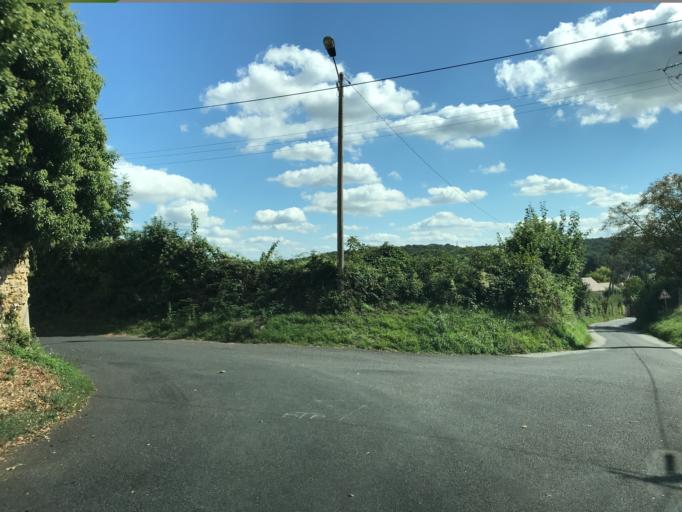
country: FR
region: Haute-Normandie
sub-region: Departement de l'Eure
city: La Chapelle-Reanville
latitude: 49.1397
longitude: 1.4014
